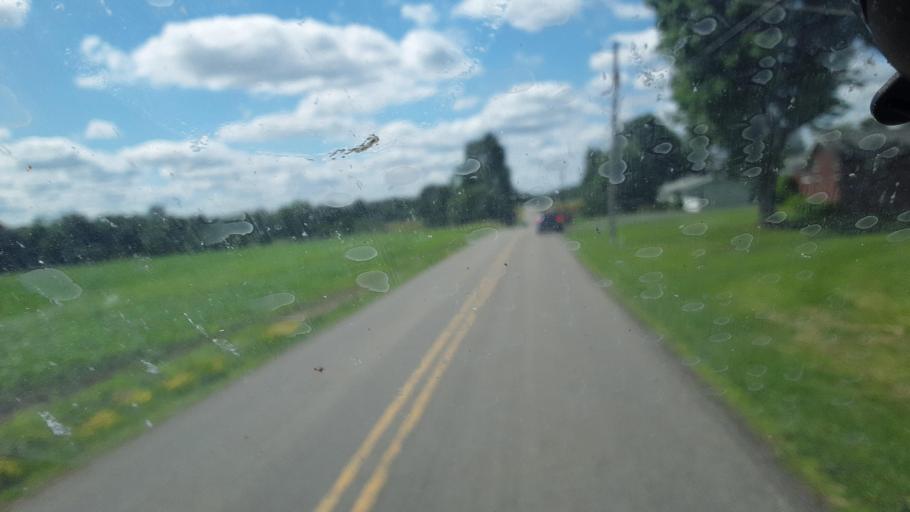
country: US
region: Pennsylvania
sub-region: Lawrence County
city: New Wilmington
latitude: 41.0716
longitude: -80.2551
